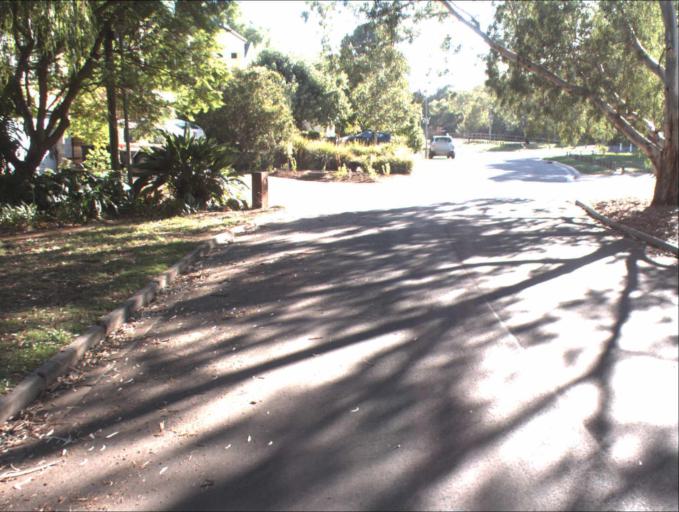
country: AU
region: South Australia
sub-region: Campbelltown
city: Paradise
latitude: -34.8727
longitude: 138.6528
